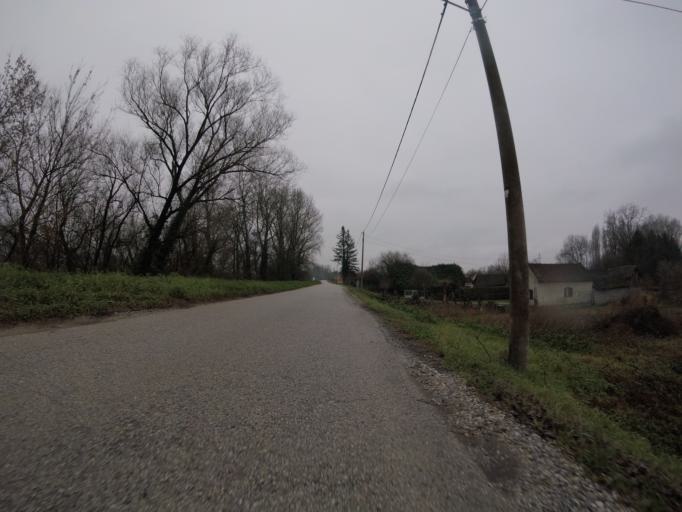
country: HR
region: Zagrebacka
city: Kuce
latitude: 45.6828
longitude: 16.2456
